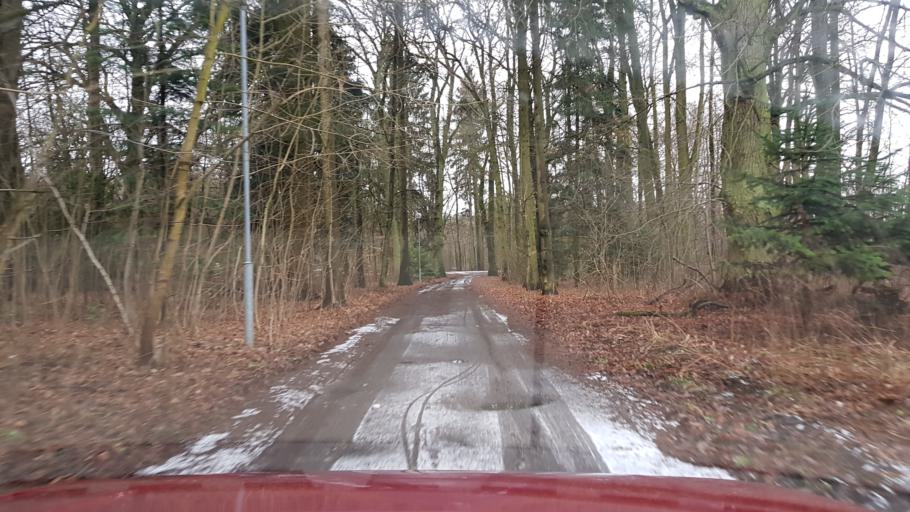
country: PL
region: West Pomeranian Voivodeship
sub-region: Powiat gryficki
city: Ploty
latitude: 53.7212
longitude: 15.3055
